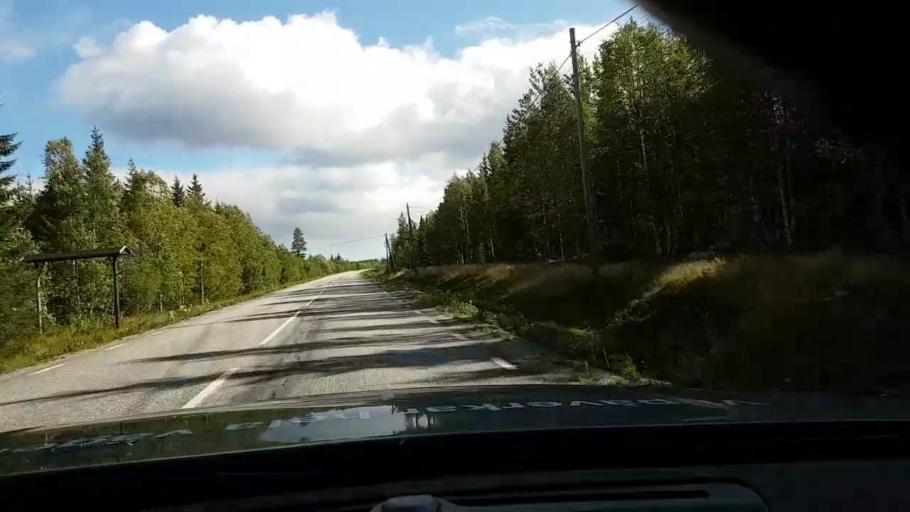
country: SE
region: Vaesterbotten
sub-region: Asele Kommun
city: Asele
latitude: 63.7818
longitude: 17.6614
